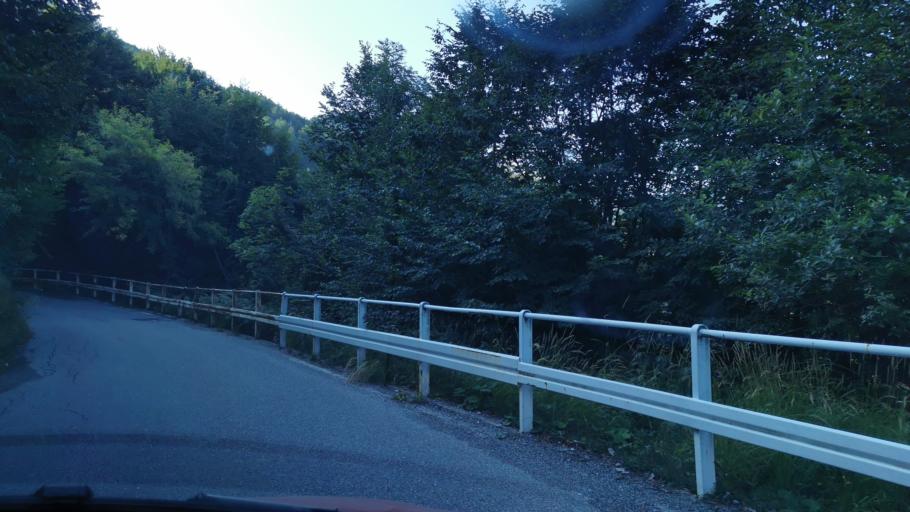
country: IT
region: Lombardy
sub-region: Provincia di Lecco
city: Moggio
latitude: 45.9142
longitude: 9.4937
